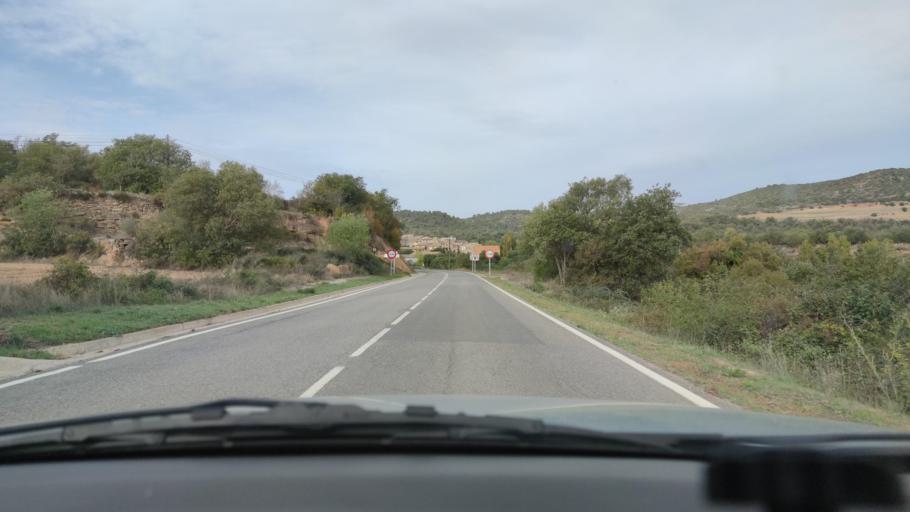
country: ES
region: Catalonia
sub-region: Provincia de Lleida
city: Artesa de Segre
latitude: 41.9241
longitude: 1.0684
